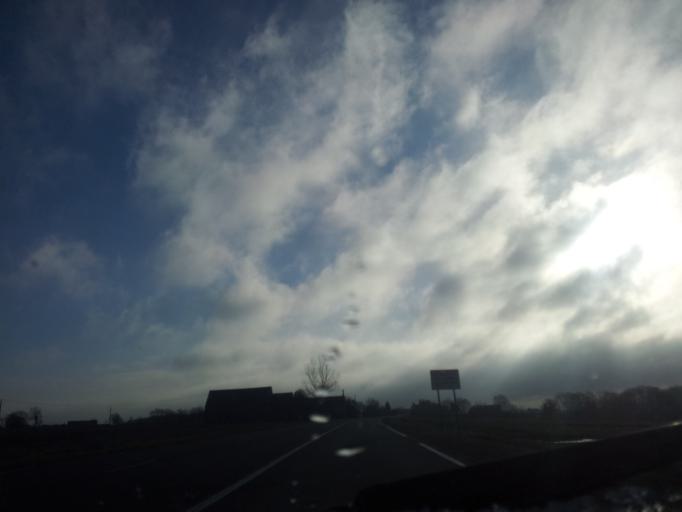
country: FR
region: Auvergne
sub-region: Departement de l'Allier
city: Chantelle
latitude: 46.3172
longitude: 3.1719
